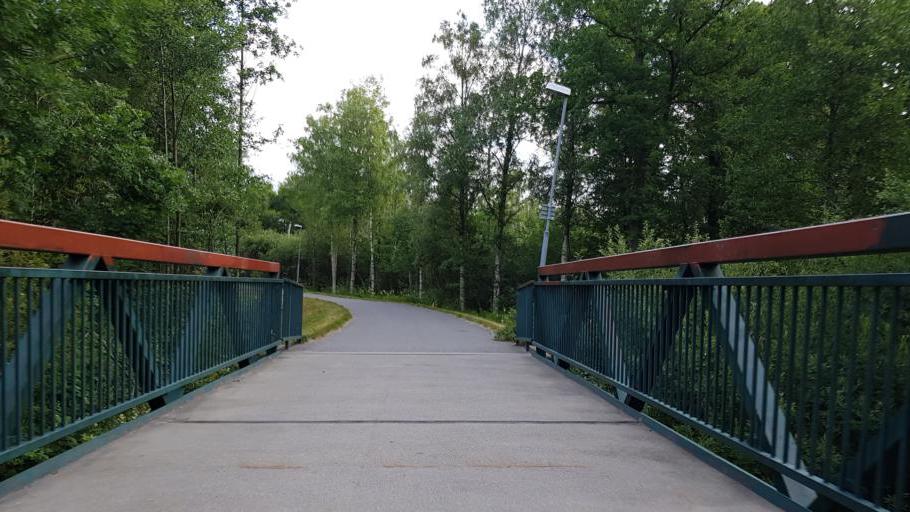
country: SE
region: Vaestra Goetaland
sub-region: Harryda Kommun
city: Molnlycke
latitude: 57.6561
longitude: 12.1094
